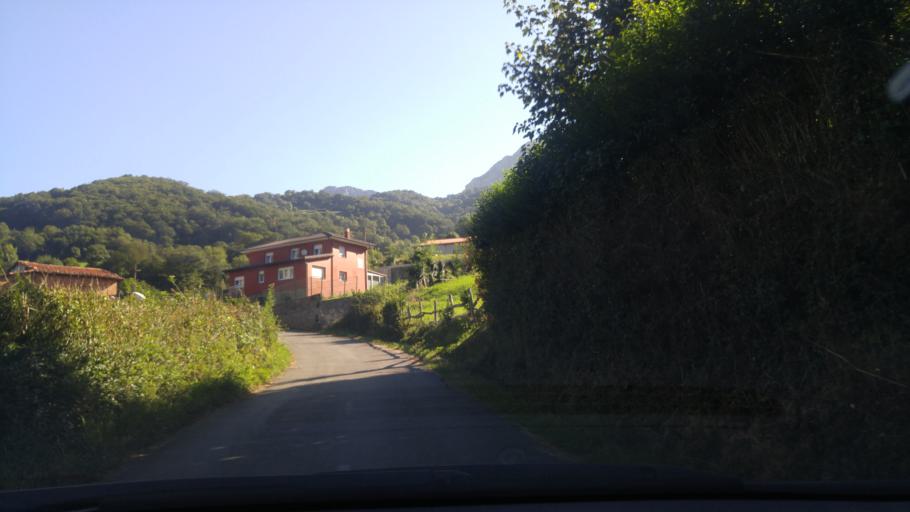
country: ES
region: Asturias
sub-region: Province of Asturias
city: Barzana
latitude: 43.1737
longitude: -5.9852
